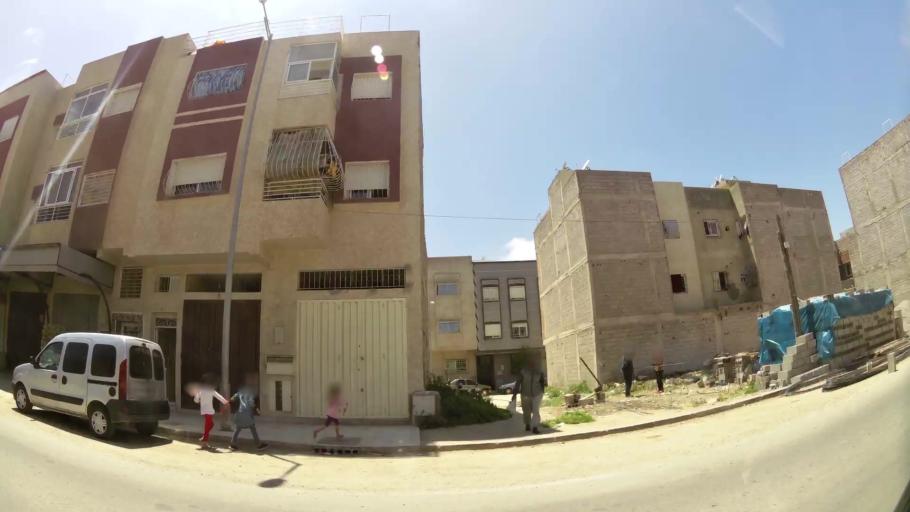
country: MA
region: Fes-Boulemane
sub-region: Fes
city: Fes
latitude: 34.0354
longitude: -5.0438
